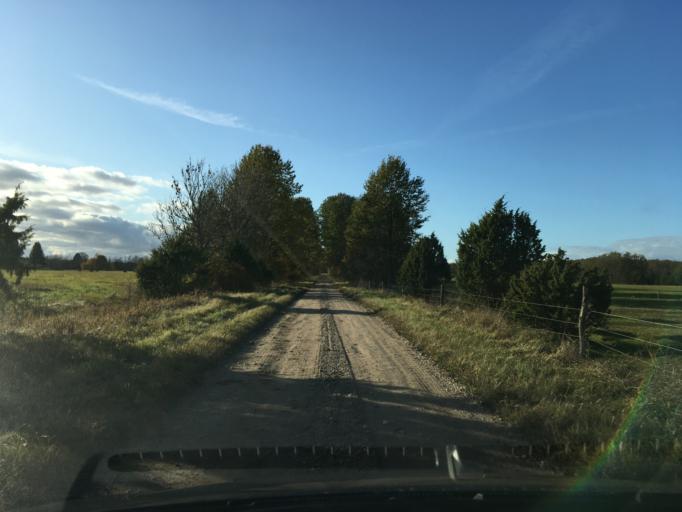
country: EE
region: Laeaene
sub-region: Lihula vald
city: Lihula
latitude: 58.5640
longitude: 23.7975
